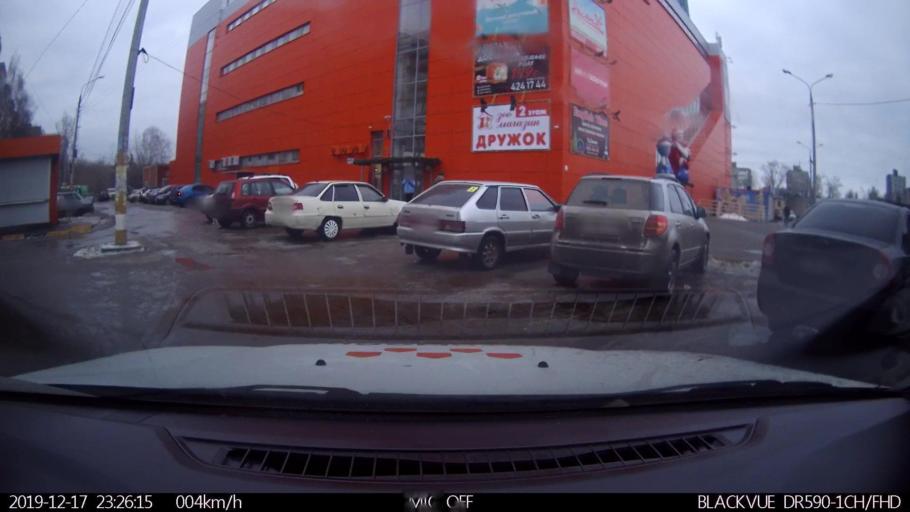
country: RU
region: Nizjnij Novgorod
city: Gorbatovka
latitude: 56.3641
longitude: 43.8150
